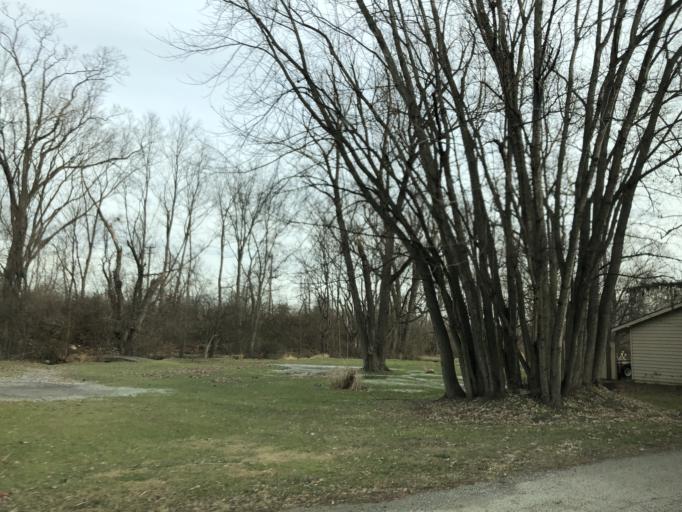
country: US
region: Pennsylvania
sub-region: Chester County
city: Exton
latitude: 40.0197
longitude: -75.6414
